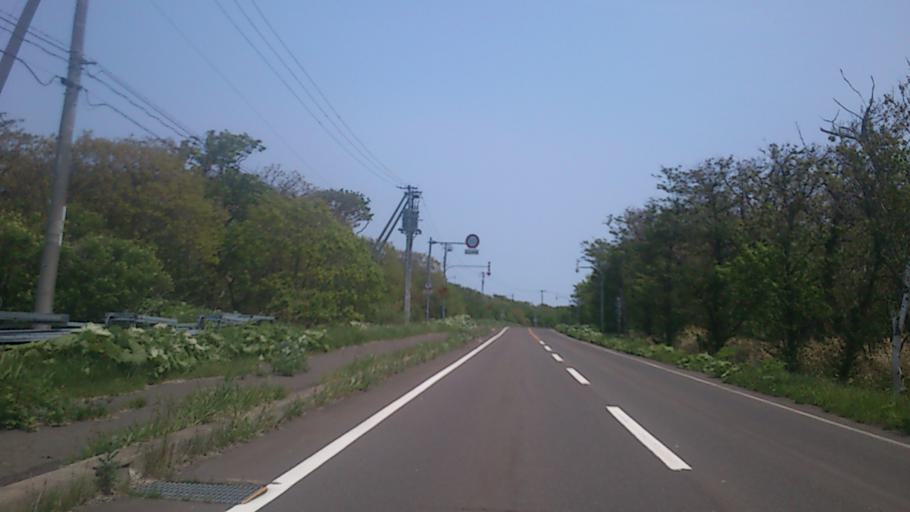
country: JP
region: Hokkaido
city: Nemuro
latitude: 43.3880
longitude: 145.6604
